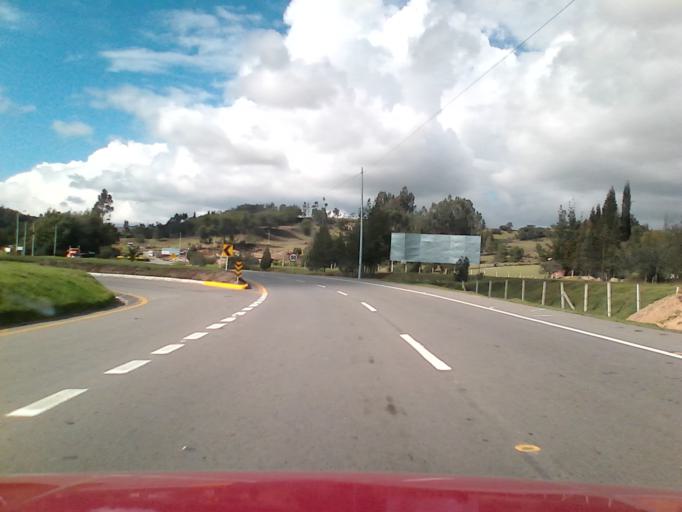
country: CO
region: Boyaca
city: Combita
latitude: 5.6524
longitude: -73.2837
